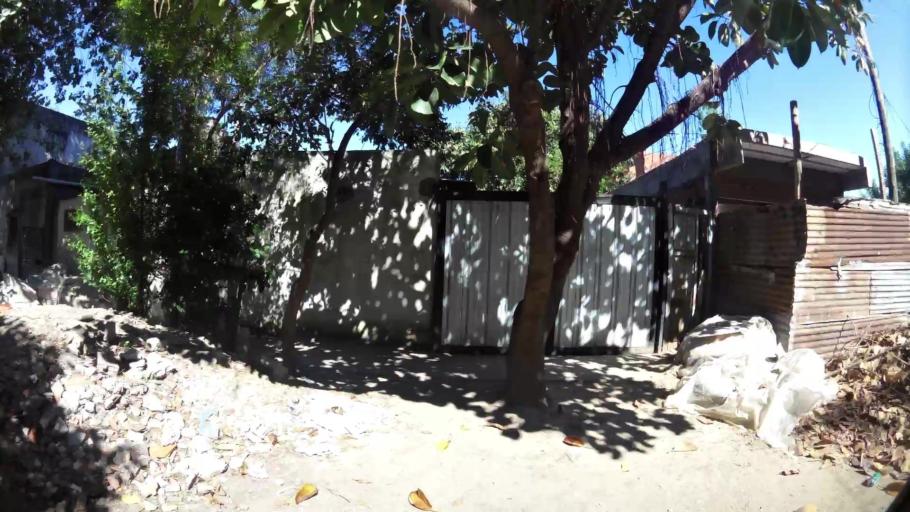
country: AR
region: Santa Fe
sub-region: Departamento de Rosario
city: Rosario
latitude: -32.9543
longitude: -60.6893
